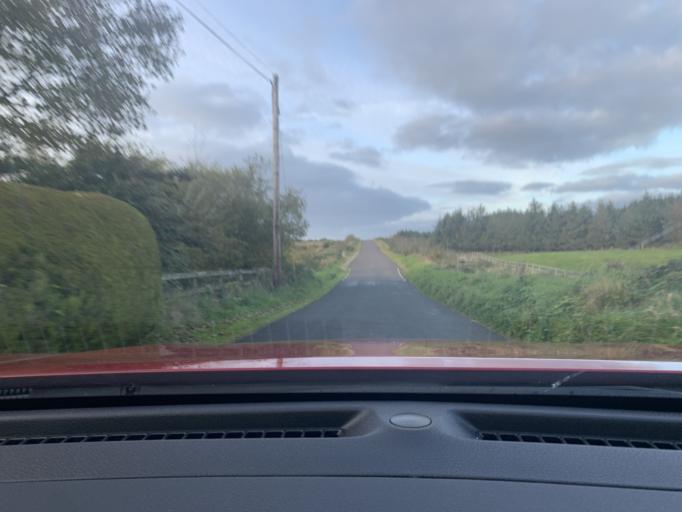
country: IE
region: Connaught
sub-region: Roscommon
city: Ballaghaderreen
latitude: 53.9187
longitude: -8.5919
